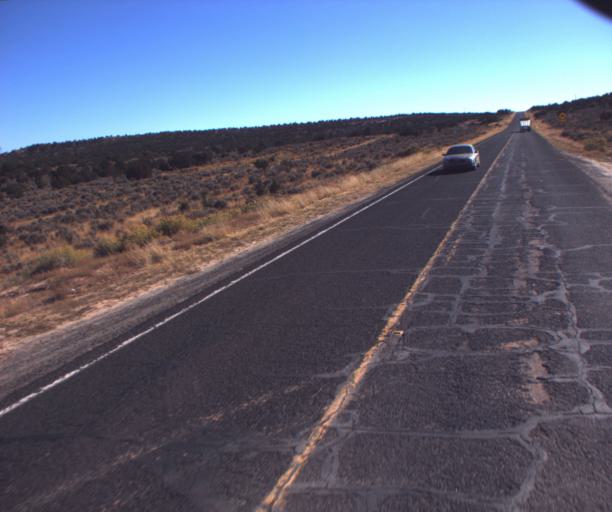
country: US
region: Arizona
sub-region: Apache County
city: Ganado
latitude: 35.6868
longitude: -109.5473
